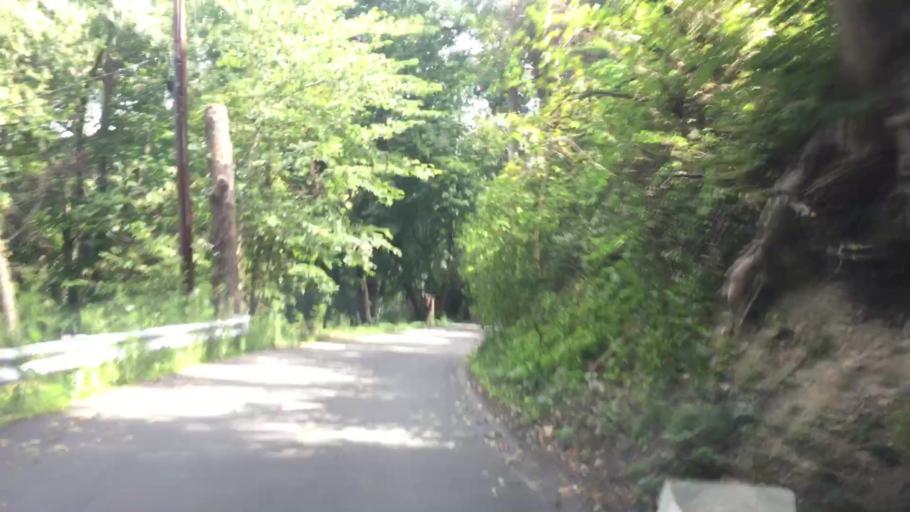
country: US
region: Pennsylvania
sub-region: Allegheny County
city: Millvale
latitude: 40.5001
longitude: -80.0024
